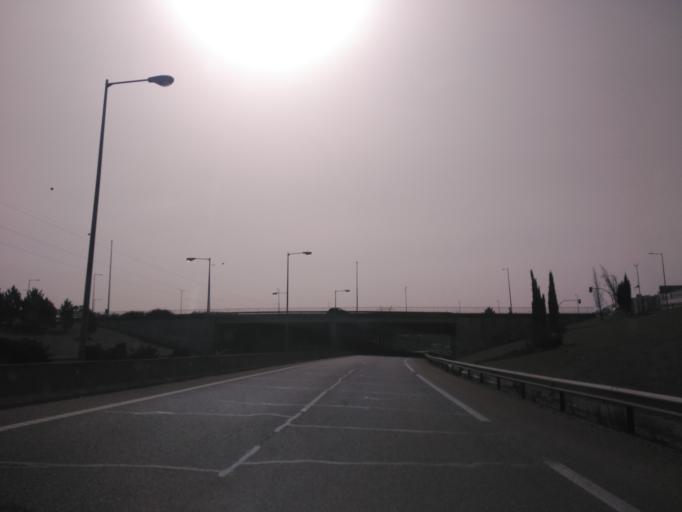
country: ES
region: Castille and Leon
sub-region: Provincia de Valladolid
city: Zaratan
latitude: 41.6623
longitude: -4.7604
